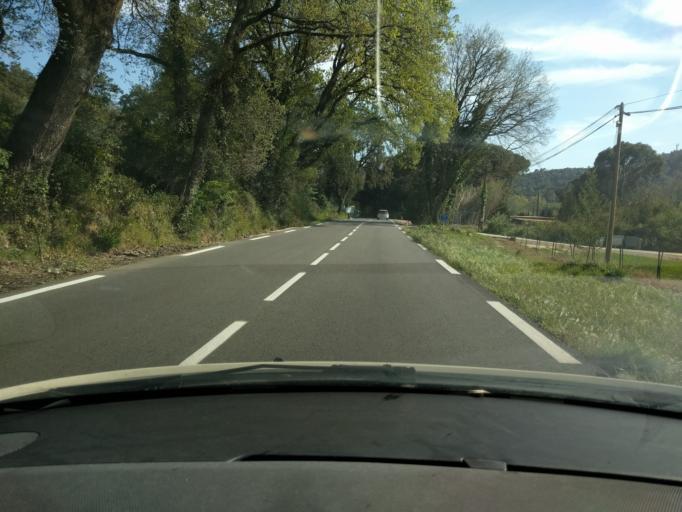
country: FR
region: Provence-Alpes-Cote d'Azur
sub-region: Departement du Var
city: La Crau
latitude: 43.1689
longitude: 6.1184
